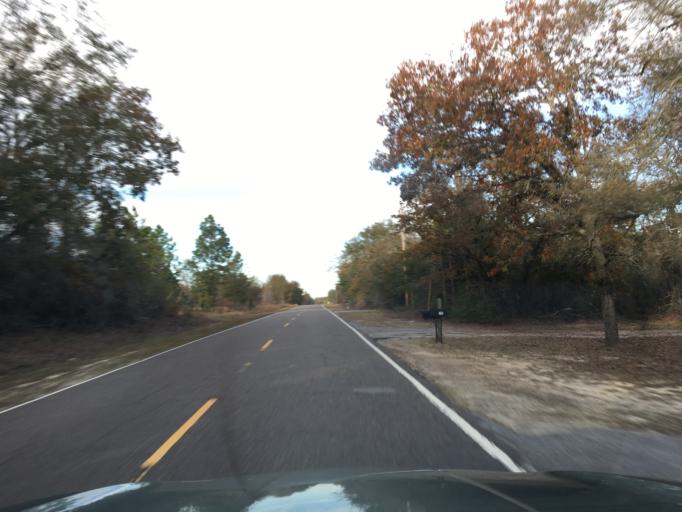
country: US
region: South Carolina
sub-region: Lexington County
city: Red Bank
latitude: 33.6960
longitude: -81.3606
